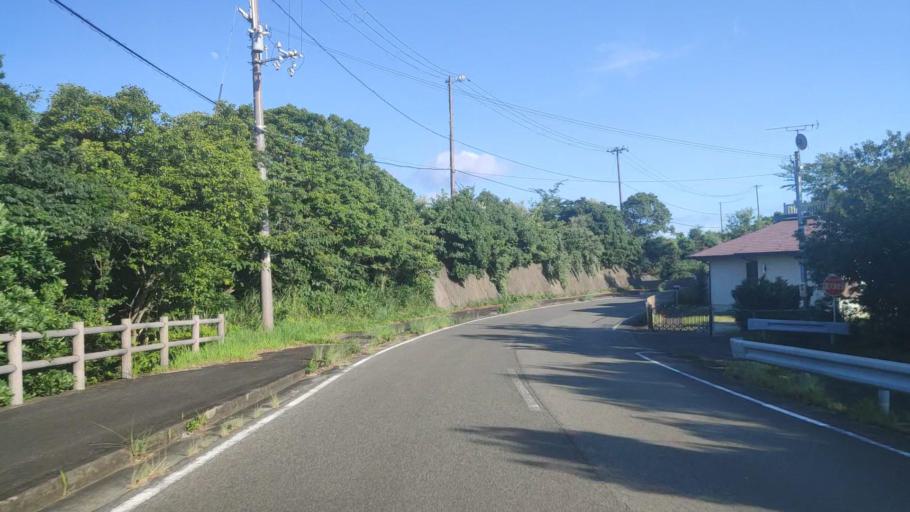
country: JP
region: Wakayama
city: Tanabe
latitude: 33.7747
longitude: 135.3055
